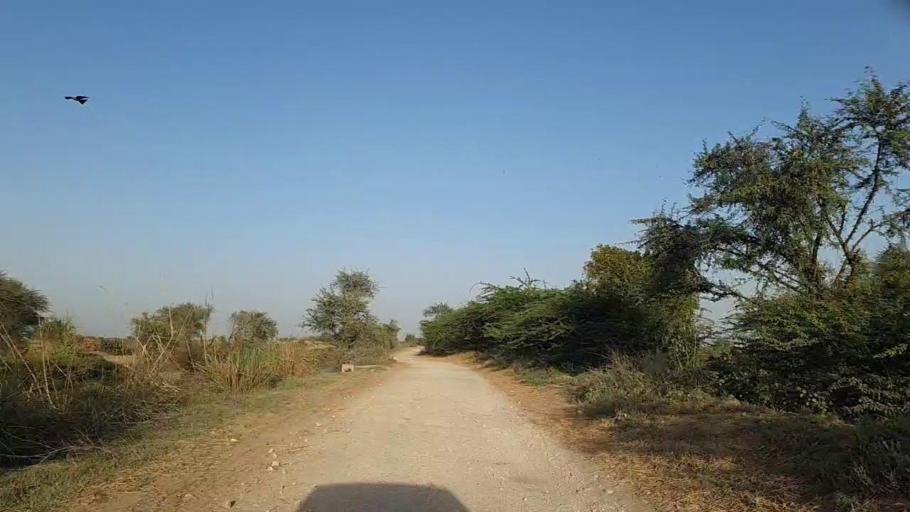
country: PK
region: Sindh
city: Jati
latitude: 24.4137
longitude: 68.3287
